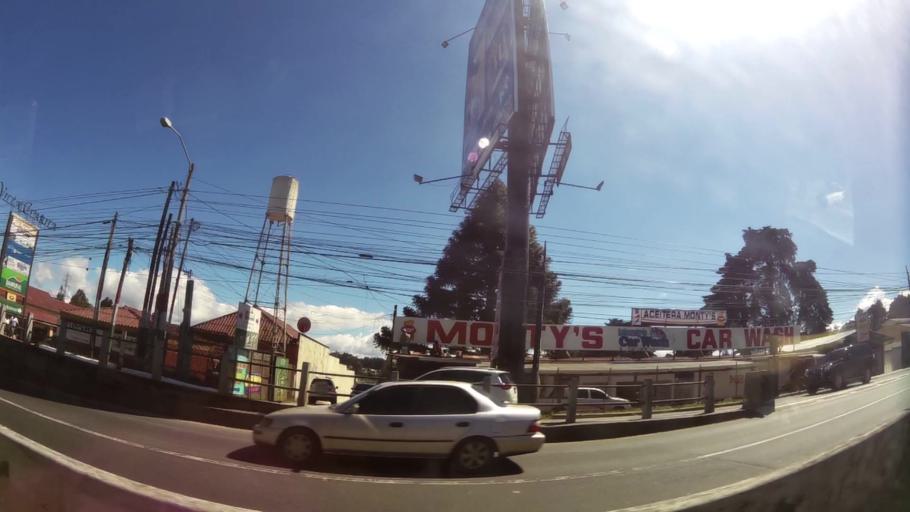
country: GT
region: Guatemala
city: San Jose Pinula
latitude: 14.5385
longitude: -90.4556
